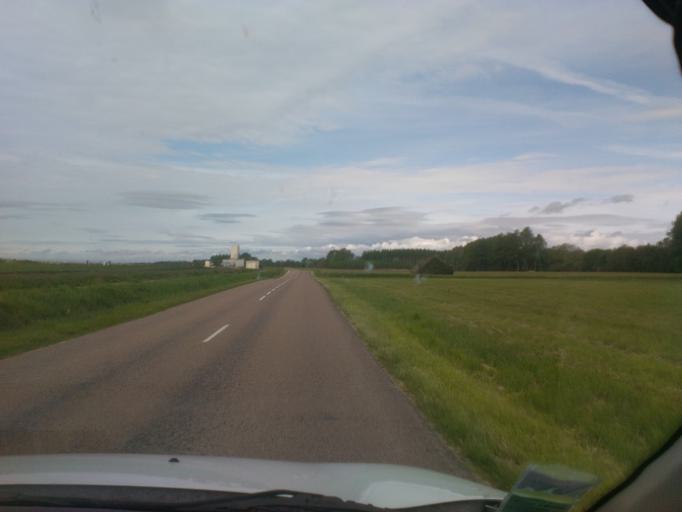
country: FR
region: Champagne-Ardenne
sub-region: Departement de l'Aube
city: Marigny-le-Chatel
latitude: 48.3561
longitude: 3.6889
